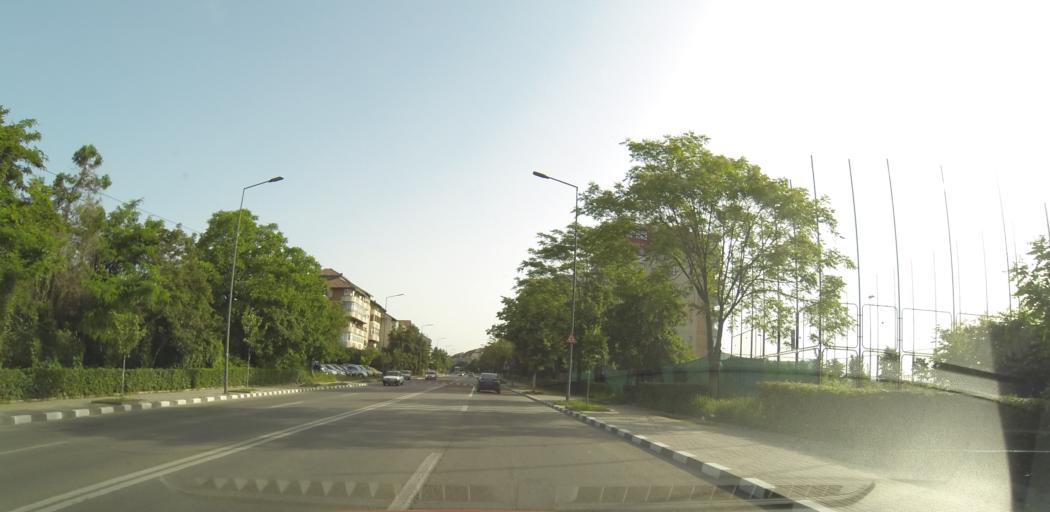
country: RO
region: Valcea
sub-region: Municipiul Ramnicu Valcea
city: Ramnicu Valcea
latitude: 45.0894
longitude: 24.3605
